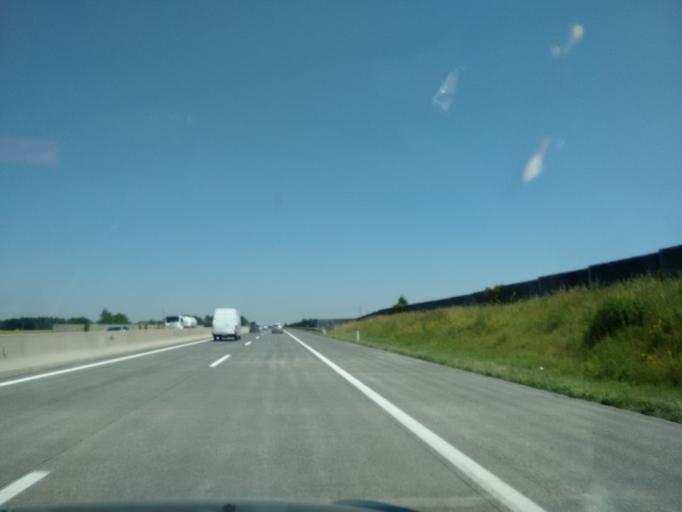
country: AT
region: Upper Austria
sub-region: Politischer Bezirk Gmunden
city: Vorchdorf
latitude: 48.0192
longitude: 13.9512
